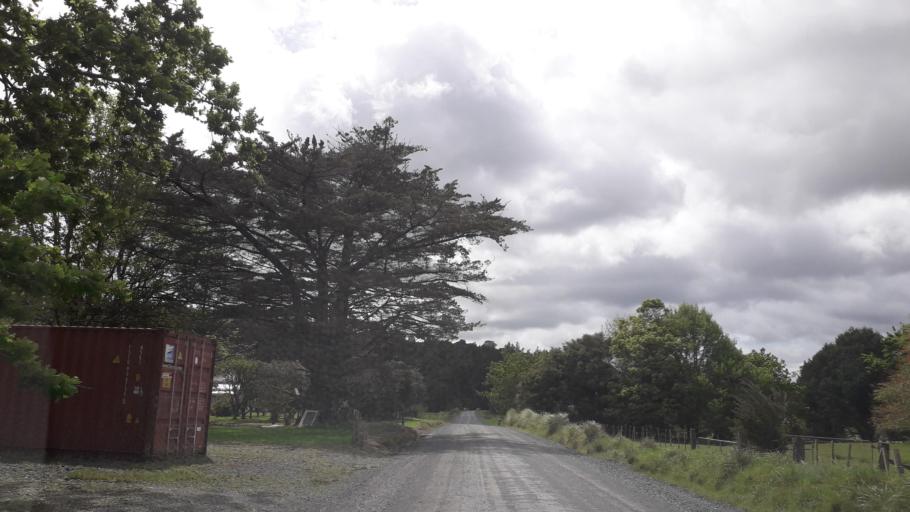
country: NZ
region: Northland
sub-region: Far North District
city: Kaitaia
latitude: -35.1724
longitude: 173.3311
